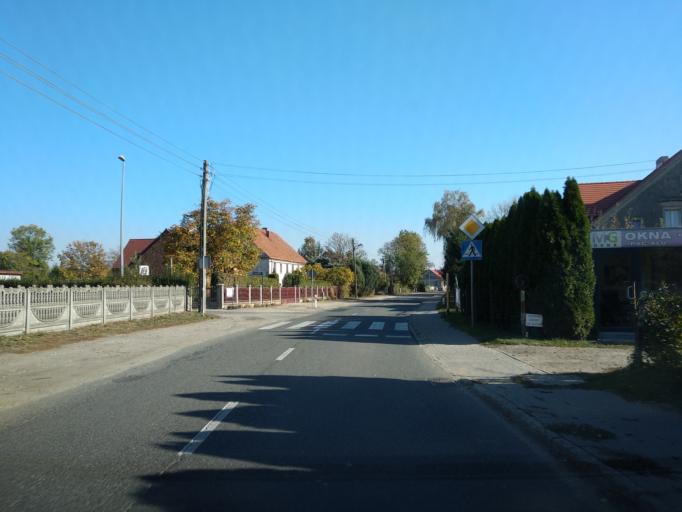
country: PL
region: Lower Silesian Voivodeship
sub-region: Powiat wroclawski
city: Bielany Wroclawskie
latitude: 51.0711
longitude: 16.9343
